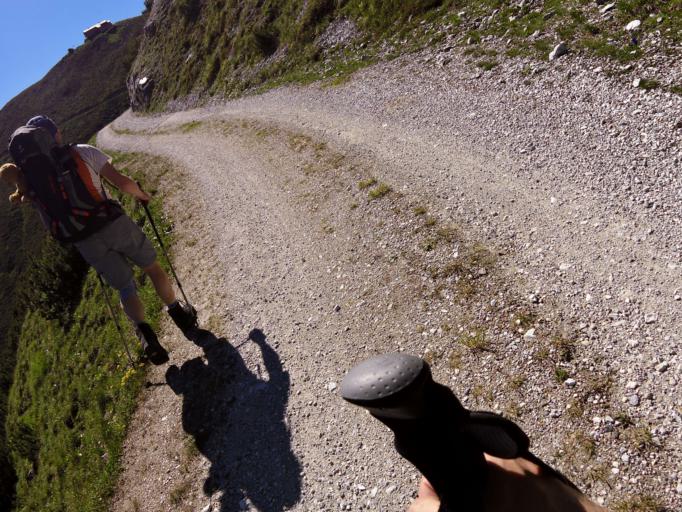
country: AT
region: Tyrol
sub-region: Politischer Bezirk Innsbruck Land
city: Neustift im Stubaital
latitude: 47.1277
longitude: 11.2862
